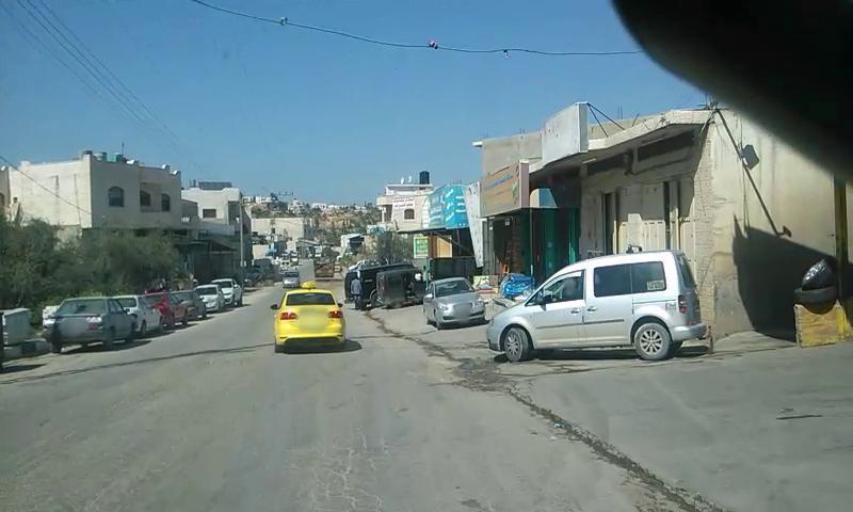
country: PS
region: West Bank
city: Idhna
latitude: 31.5639
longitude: 34.9788
